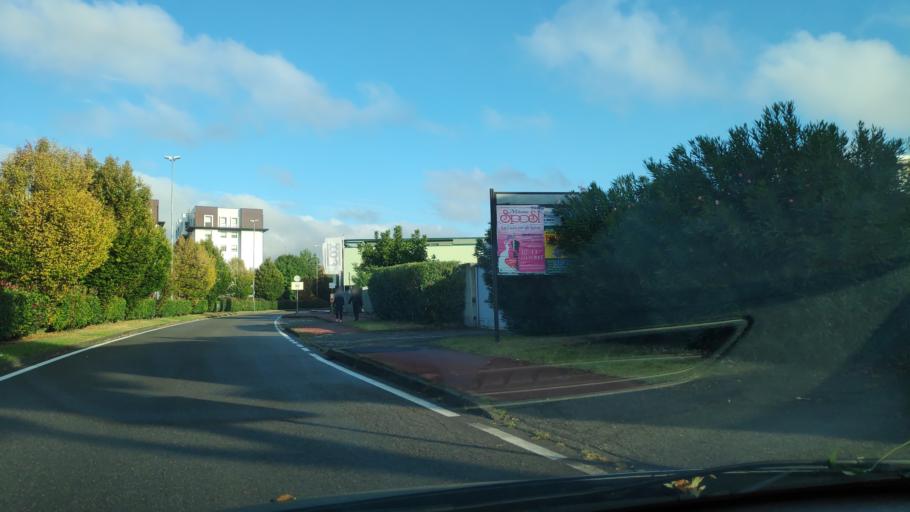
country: IT
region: Lombardy
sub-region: Citta metropolitana di Milano
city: Opera
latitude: 45.3700
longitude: 9.2142
